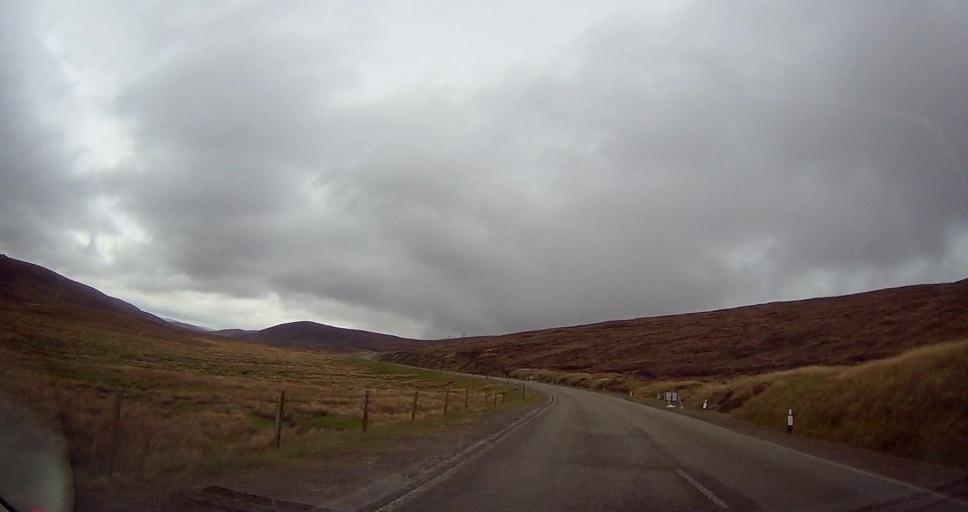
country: GB
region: Scotland
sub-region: Shetland Islands
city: Lerwick
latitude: 60.2853
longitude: -1.2423
